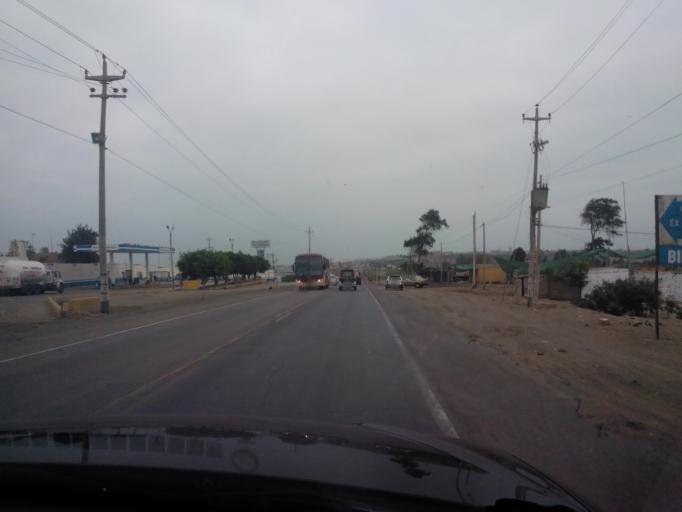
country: PE
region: Ica
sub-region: Provincia de Pisco
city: Villa Tupac Amaru
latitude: -13.6993
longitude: -76.1518
